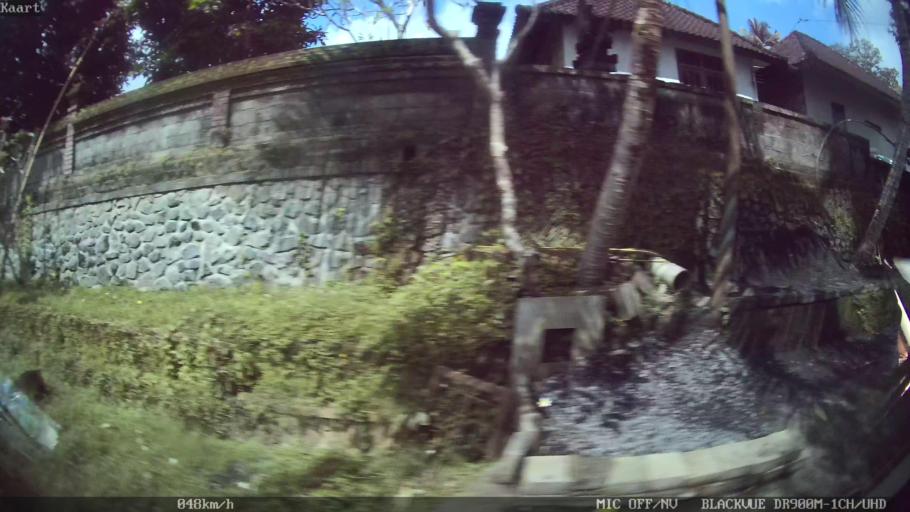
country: ID
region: Bali
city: Banjar Mulung
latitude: -8.4930
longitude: 115.3207
